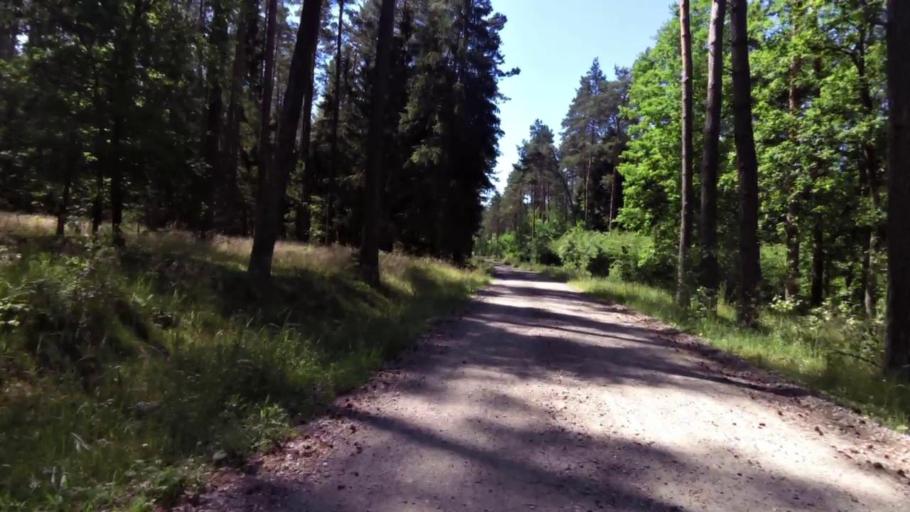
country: PL
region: West Pomeranian Voivodeship
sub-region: Powiat swidwinski
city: Rabino
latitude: 53.9145
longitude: 16.0066
